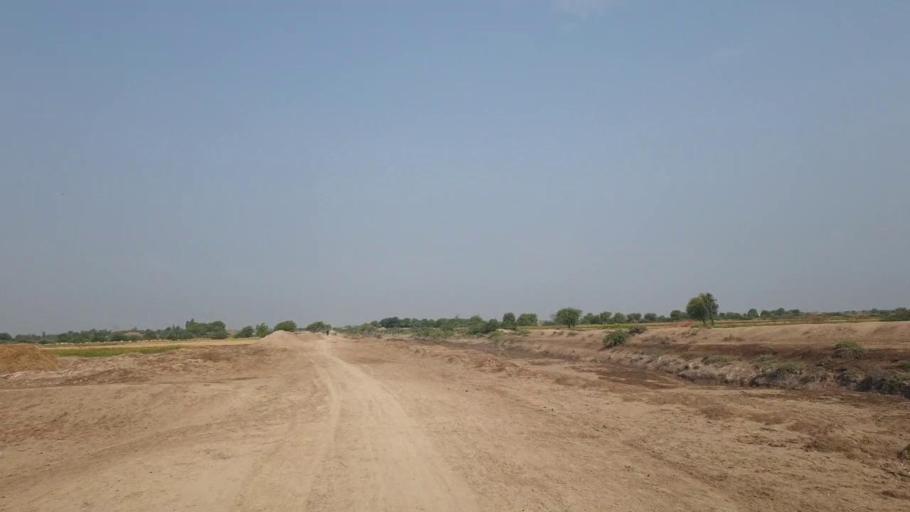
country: PK
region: Sindh
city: Badin
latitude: 24.7305
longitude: 68.7676
